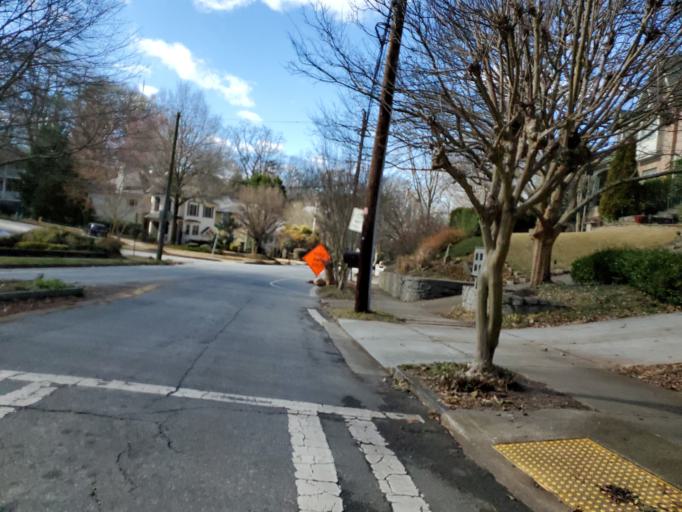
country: US
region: Georgia
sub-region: DeKalb County
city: Druid Hills
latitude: 33.7645
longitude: -84.3223
